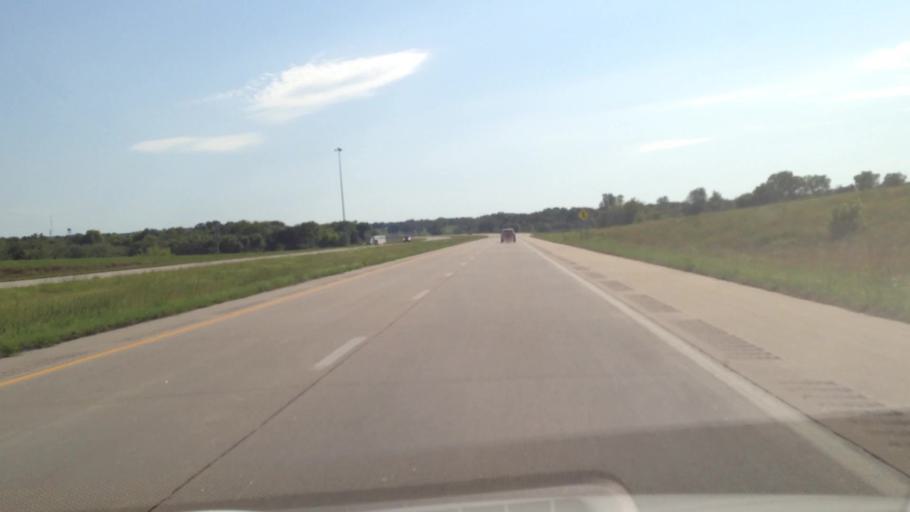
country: US
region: Kansas
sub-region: Linn County
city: Pleasanton
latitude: 38.1458
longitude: -94.7074
